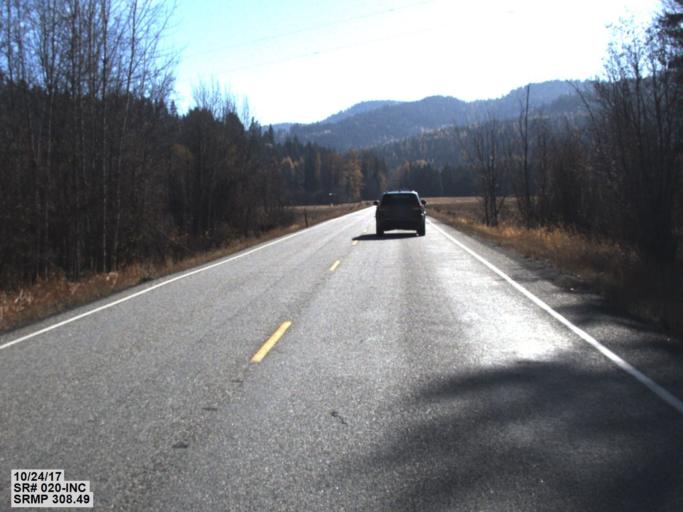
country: US
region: Washington
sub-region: Ferry County
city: Republic
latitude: 48.6083
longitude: -118.6599
